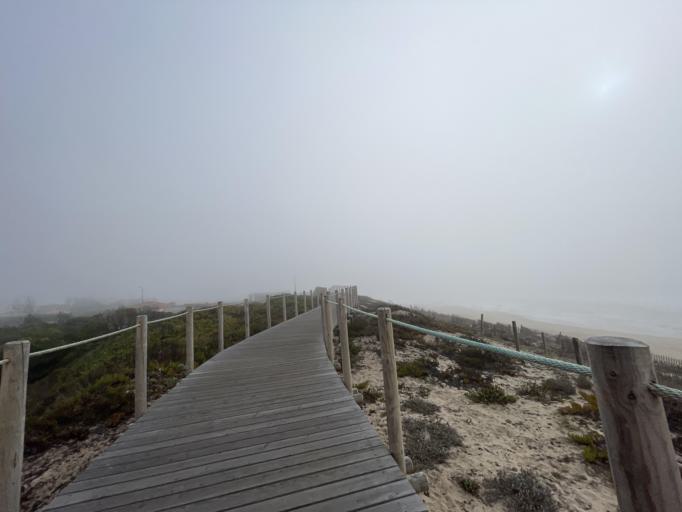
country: PT
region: Porto
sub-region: Vila Nova de Gaia
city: Vila Nova da Telha
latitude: 41.0866
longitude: -8.6566
